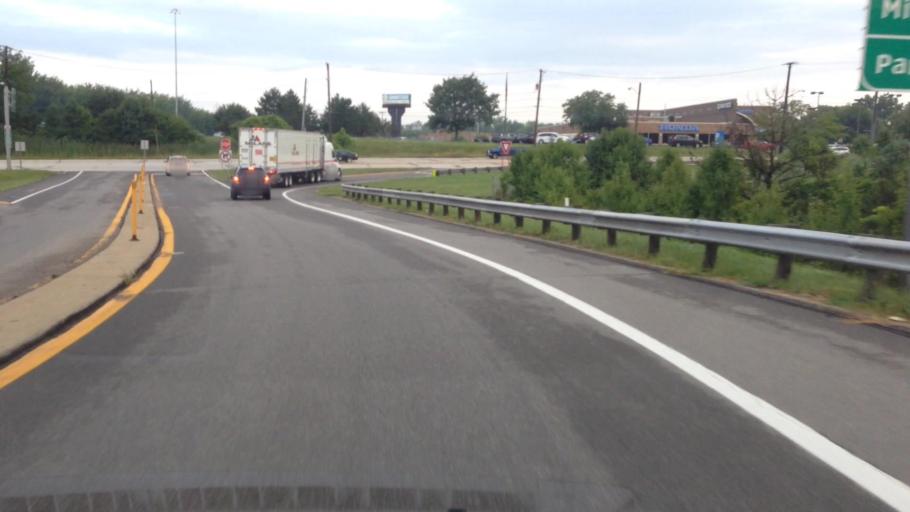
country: US
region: Ohio
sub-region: Cuyahoga County
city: Middleburg Heights
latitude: 41.3561
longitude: -81.8172
